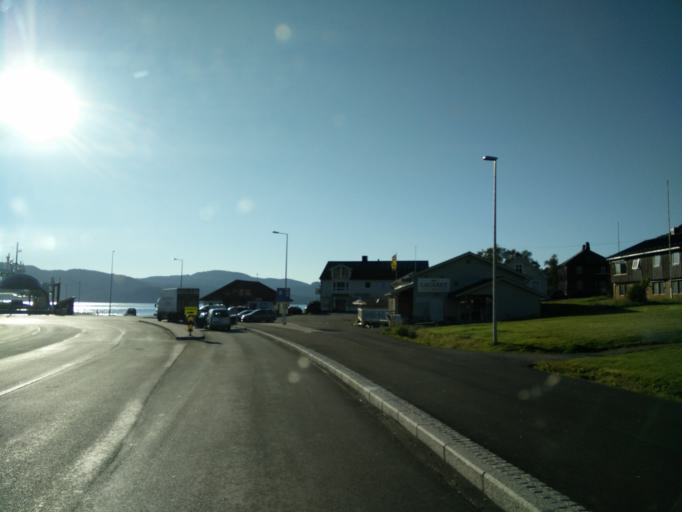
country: NO
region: More og Romsdal
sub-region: Halsa
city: Liaboen
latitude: 63.0685
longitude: 8.2295
